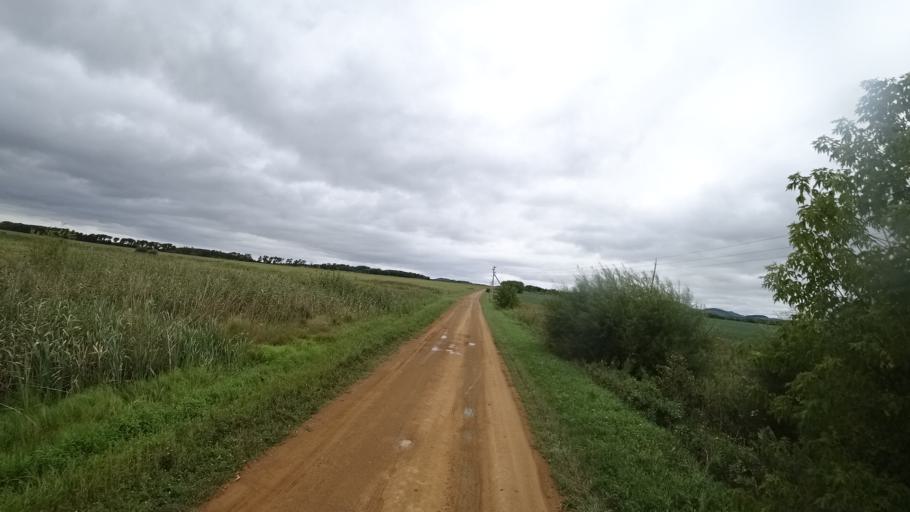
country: RU
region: Primorskiy
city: Chernigovka
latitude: 44.4342
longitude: 132.5924
